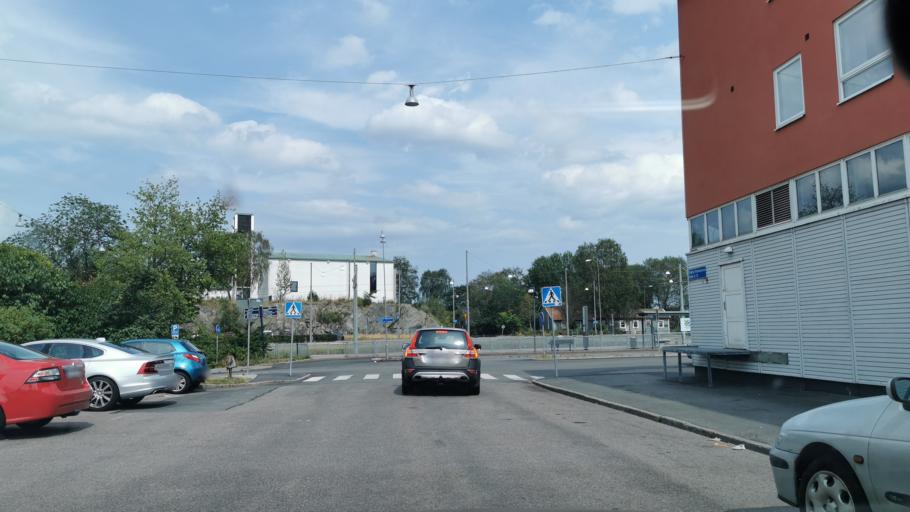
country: SE
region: Vaestra Goetaland
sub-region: Goteborg
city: Goeteborg
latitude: 57.6843
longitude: 11.9717
